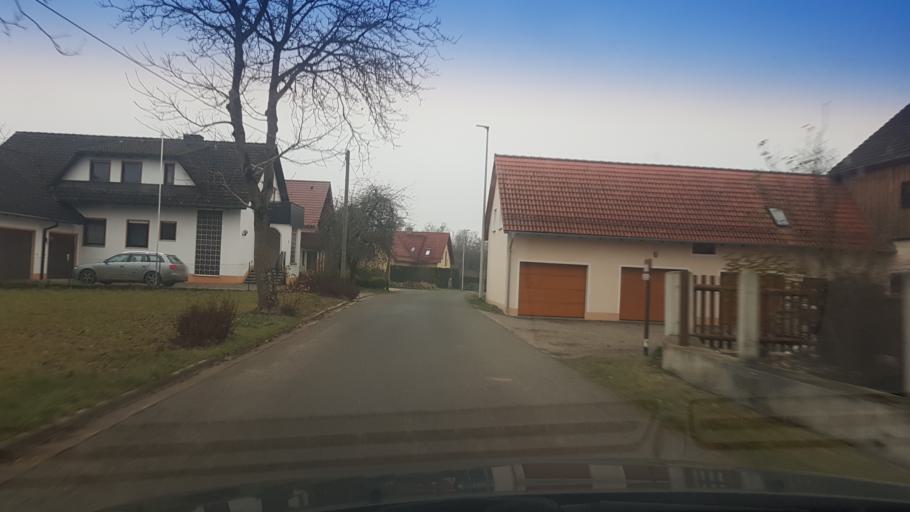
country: DE
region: Bavaria
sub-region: Upper Franconia
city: Wonsees
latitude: 50.0341
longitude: 11.2903
